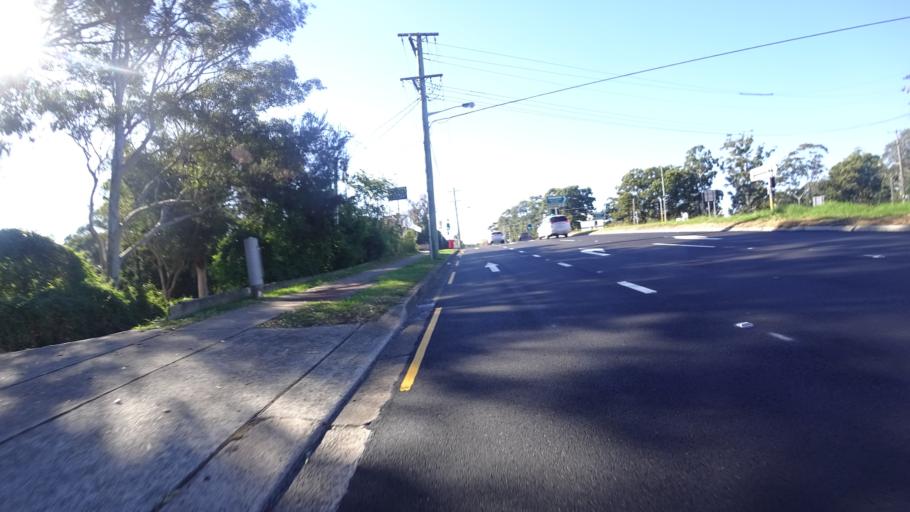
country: AU
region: New South Wales
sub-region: The Hills Shire
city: Castle Hill
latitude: -33.7312
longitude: 151.0163
